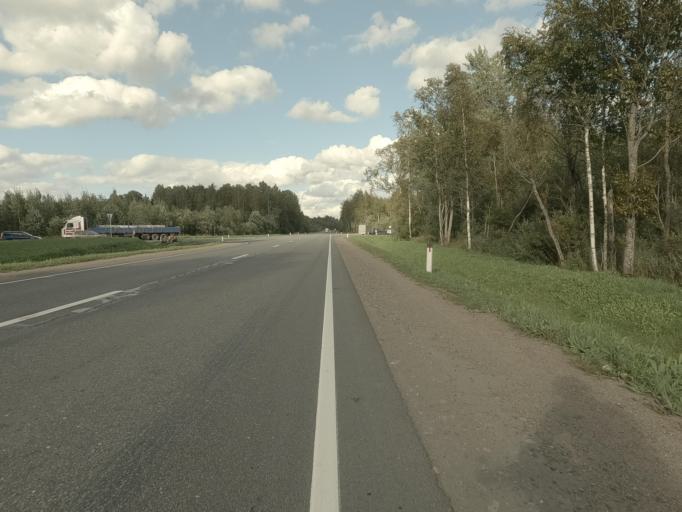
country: RU
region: Leningrad
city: Nikol'skoye
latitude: 59.6618
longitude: 30.8746
